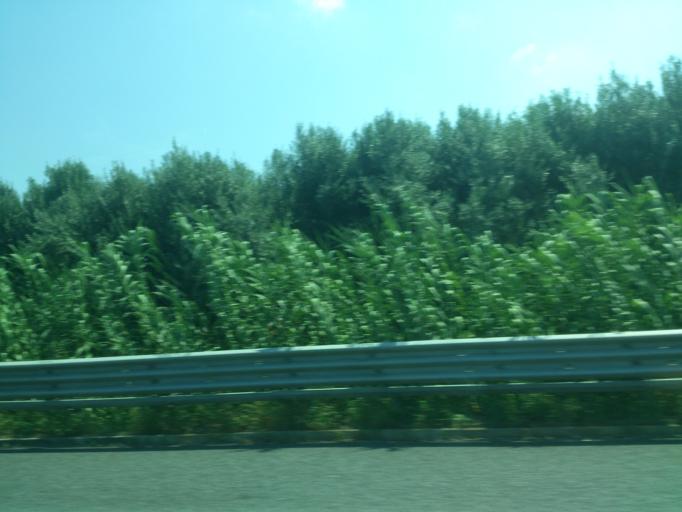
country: IT
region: Calabria
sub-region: Provincia di Vibo-Valentia
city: Francavilla Angitola
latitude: 38.8015
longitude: 16.2296
